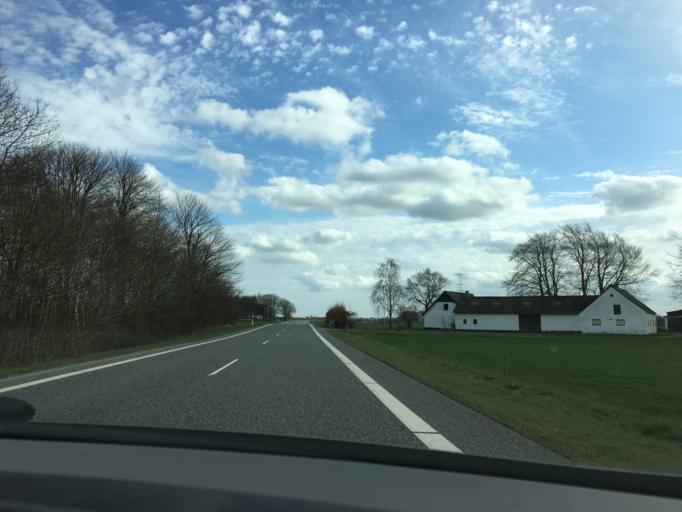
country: DK
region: South Denmark
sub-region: Vejle Kommune
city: Jelling
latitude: 55.7899
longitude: 9.3880
